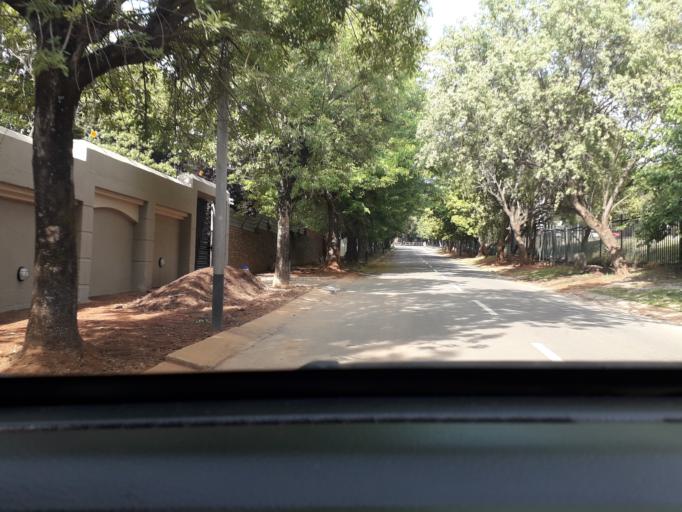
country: ZA
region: Gauteng
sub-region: City of Johannesburg Metropolitan Municipality
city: Modderfontein
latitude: -26.0920
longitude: 28.0594
